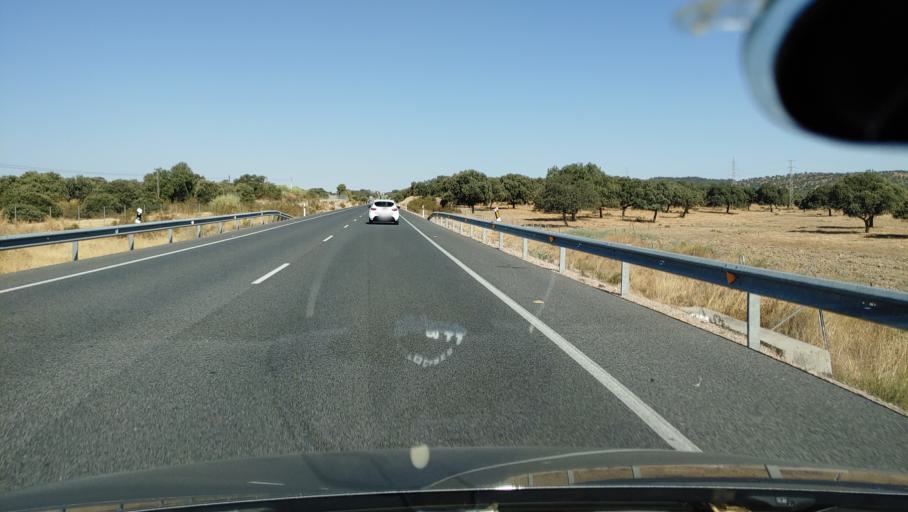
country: ES
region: Andalusia
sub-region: Province of Cordoba
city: Obejo
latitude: 38.0630
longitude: -4.8253
